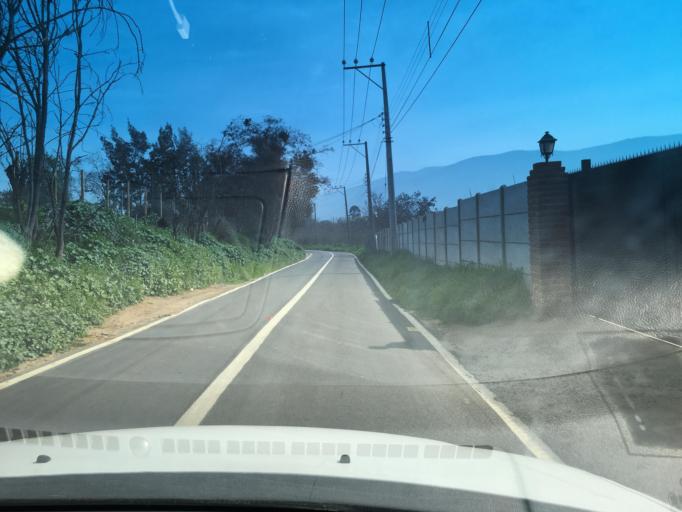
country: CL
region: Valparaiso
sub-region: Provincia de Marga Marga
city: Limache
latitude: -33.0079
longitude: -71.2212
